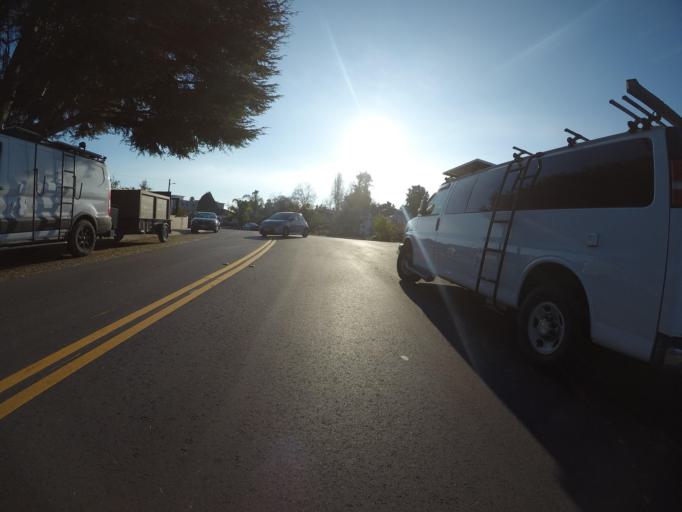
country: US
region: California
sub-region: Santa Cruz County
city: Santa Cruz
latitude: 36.9626
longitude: -122.0487
